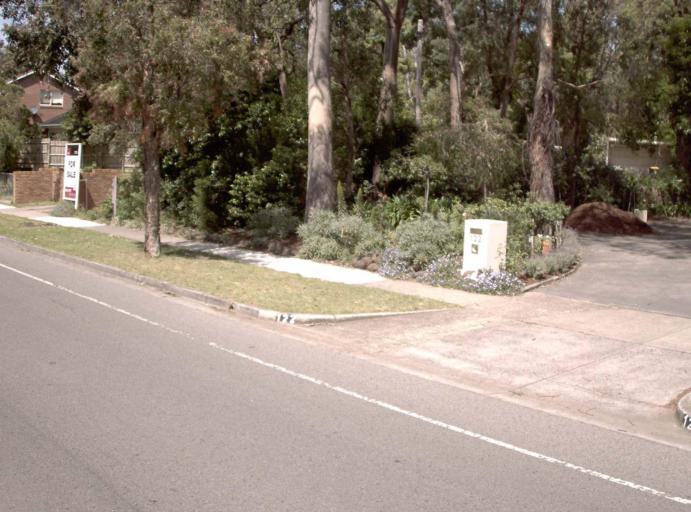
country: AU
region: Victoria
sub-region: Whitehorse
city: Blackburn South
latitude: -37.8304
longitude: 145.1545
